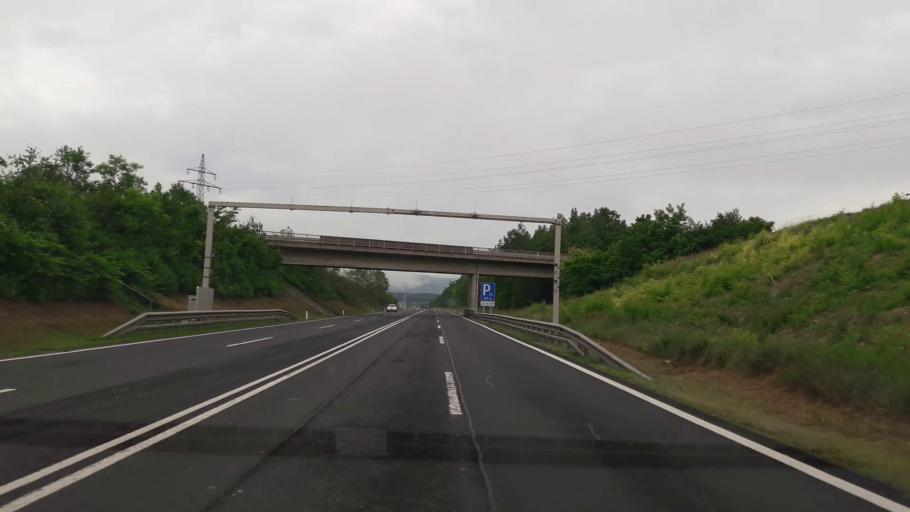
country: AT
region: Burgenland
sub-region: Politischer Bezirk Mattersburg
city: Mattersburg
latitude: 47.7459
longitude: 16.3825
